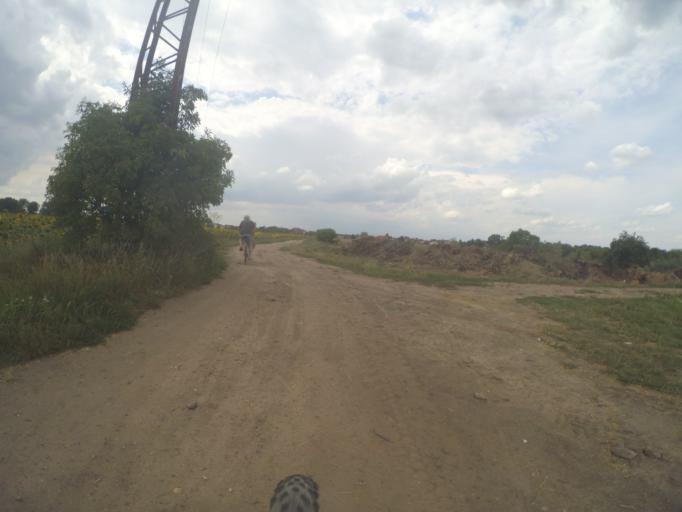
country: CZ
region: Central Bohemia
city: Libis
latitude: 50.2888
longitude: 14.4859
